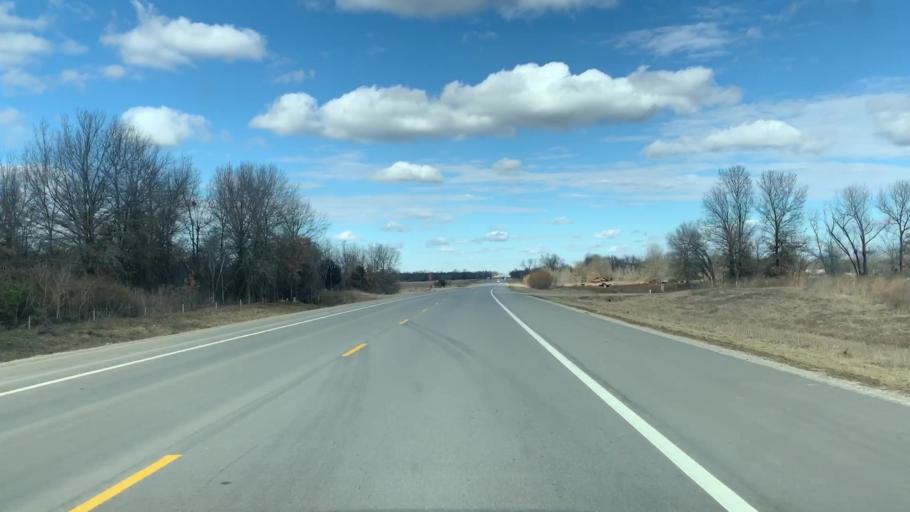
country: US
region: Kansas
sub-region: Cherokee County
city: Columbus
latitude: 37.2609
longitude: -94.8320
